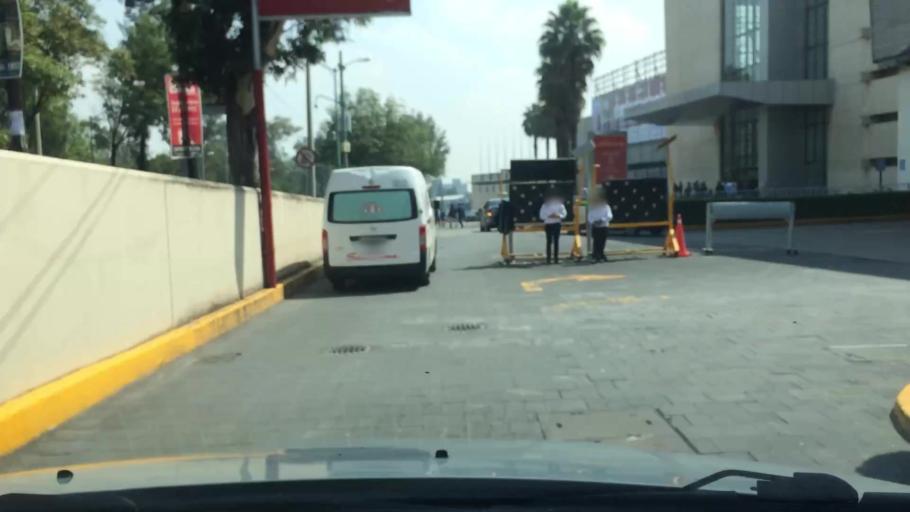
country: MX
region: Mexico City
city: Miguel Hidalgo
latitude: 19.4414
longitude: -99.2237
